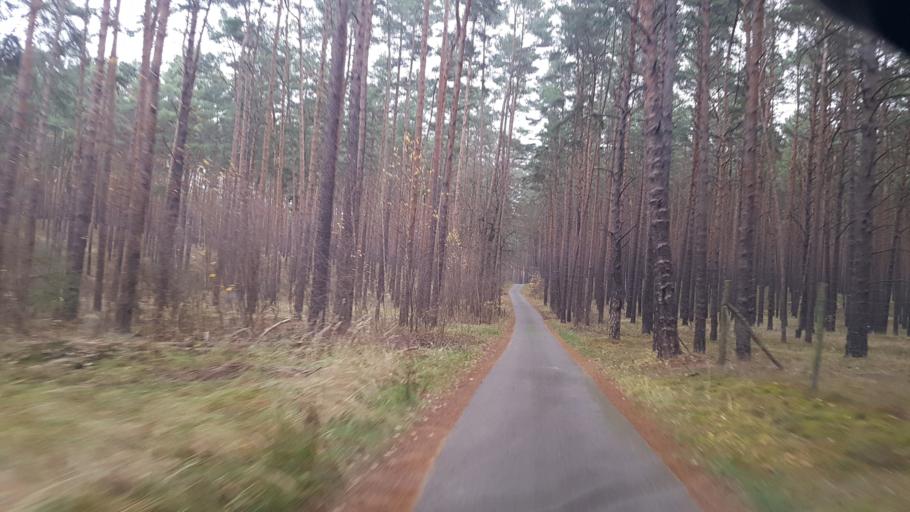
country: DE
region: Brandenburg
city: Schenkendobern
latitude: 51.9764
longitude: 14.6547
